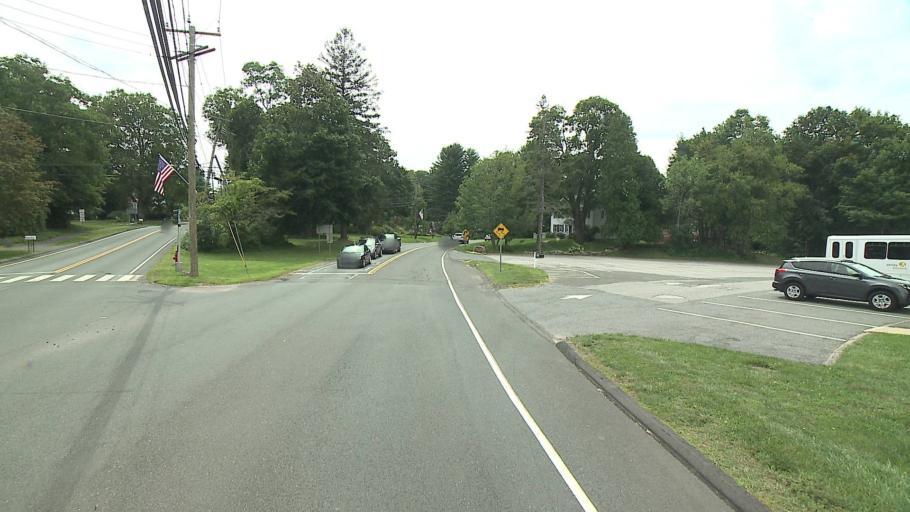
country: US
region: Connecticut
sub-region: Fairfield County
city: Danbury
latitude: 41.4657
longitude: -73.3876
